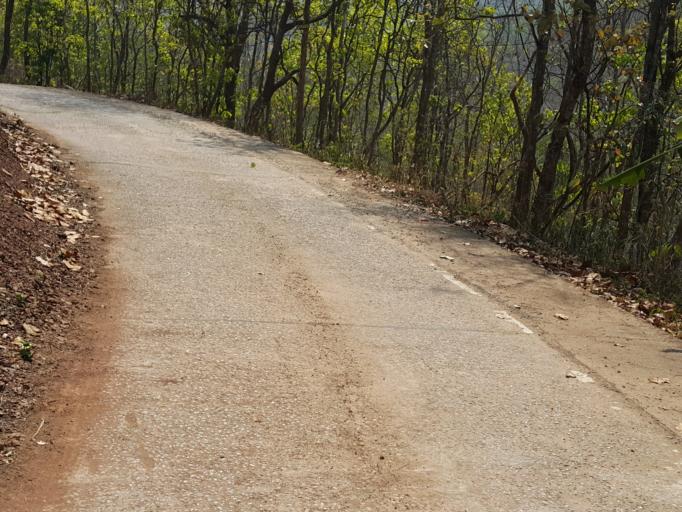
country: TH
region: Lampang
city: Chae Hom
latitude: 18.7494
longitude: 99.5410
